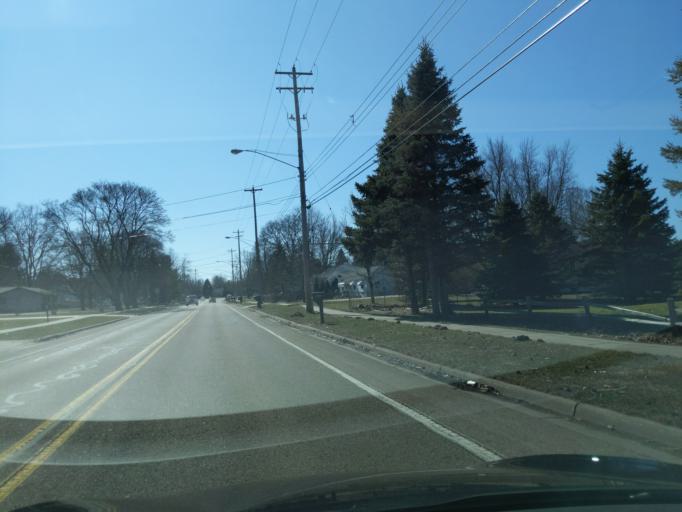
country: US
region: Michigan
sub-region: Ingham County
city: Holt
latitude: 42.6573
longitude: -84.5646
